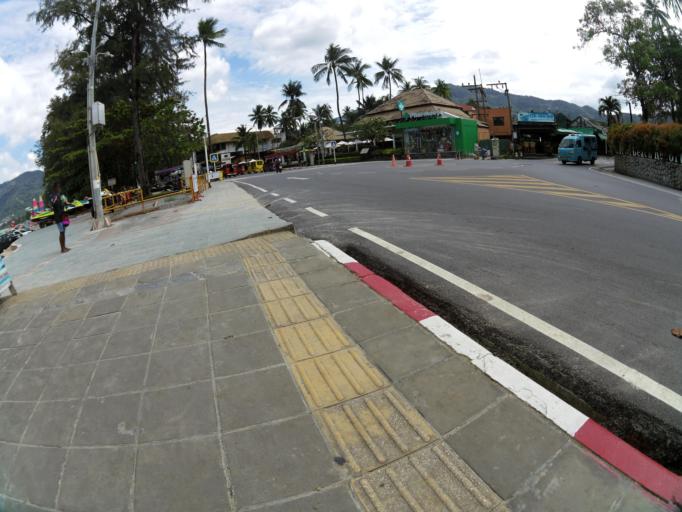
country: TH
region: Phuket
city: Patong
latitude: 7.8874
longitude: 98.2910
